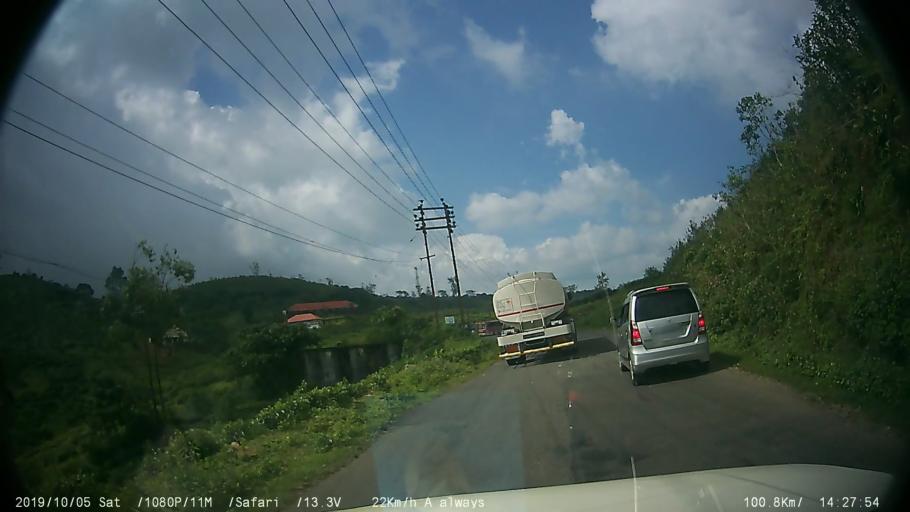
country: IN
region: Kerala
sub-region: Kottayam
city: Erattupetta
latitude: 9.6047
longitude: 76.9664
